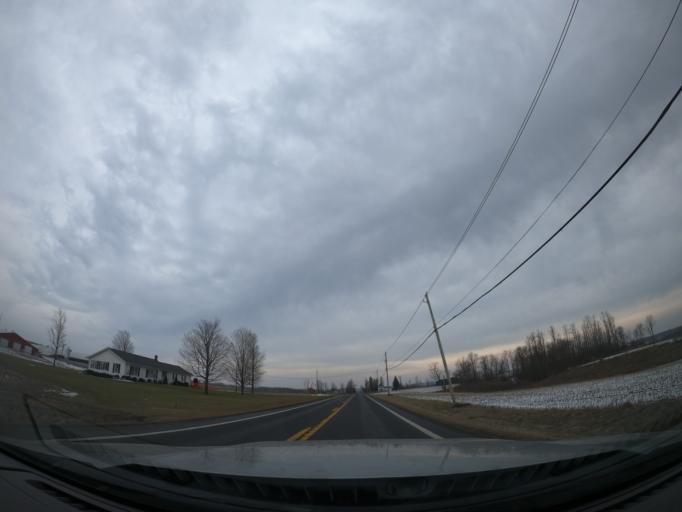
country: US
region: New York
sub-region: Cayuga County
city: Melrose Park
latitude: 42.7751
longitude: -76.5584
